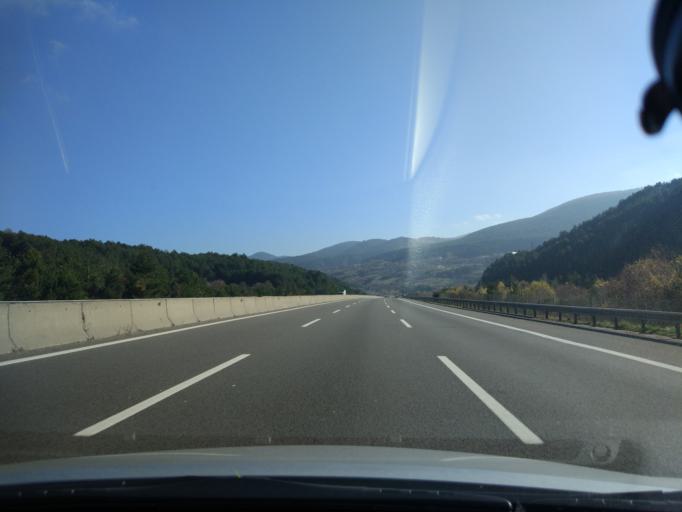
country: TR
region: Bolu
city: Bolu
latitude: 40.7387
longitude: 31.7936
